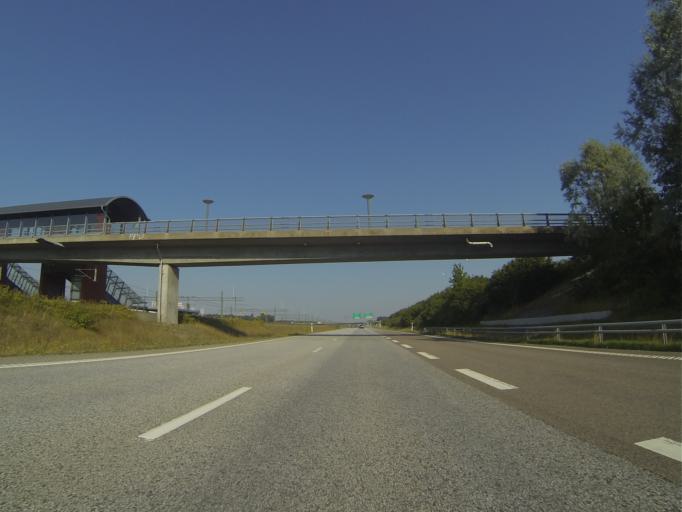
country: SE
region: Skane
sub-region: Malmo
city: Tygelsjo
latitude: 55.5468
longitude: 12.9905
